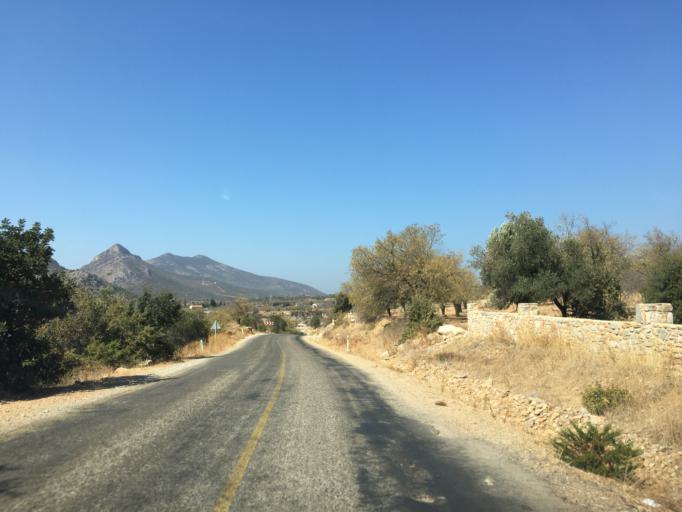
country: TR
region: Mugla
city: Datca
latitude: 36.6946
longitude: 27.4704
